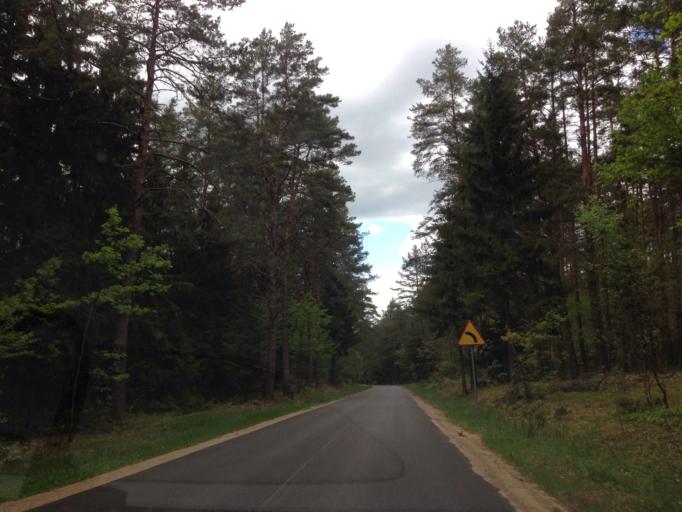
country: PL
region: Podlasie
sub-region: Powiat moniecki
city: Goniadz
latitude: 53.3589
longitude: 22.5994
